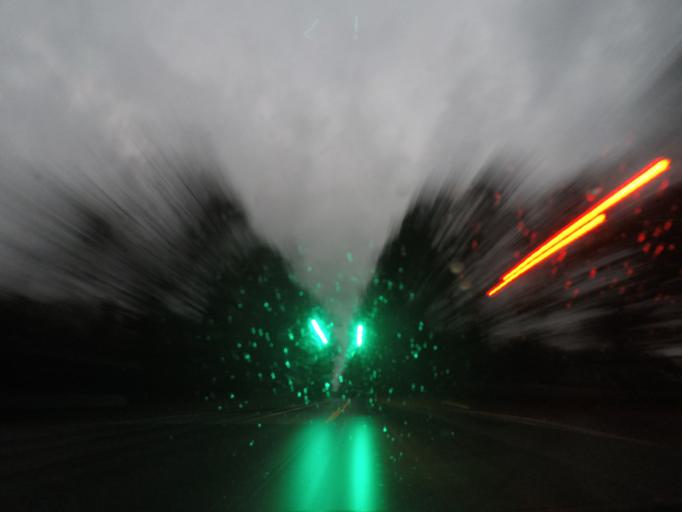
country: US
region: North Carolina
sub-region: Orange County
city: Hillsborough
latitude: 36.0694
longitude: -79.0631
